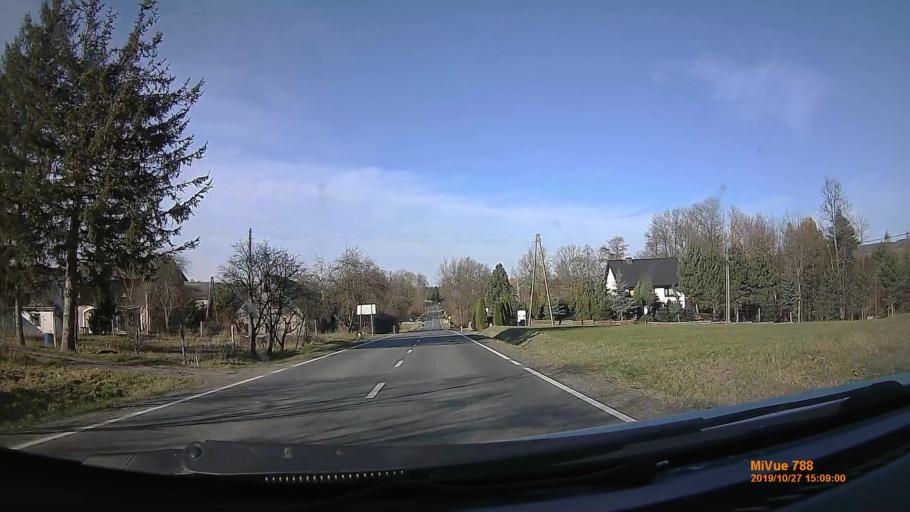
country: PL
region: Lower Silesian Voivodeship
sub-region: Powiat klodzki
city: Miedzylesie
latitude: 50.1759
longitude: 16.6697
